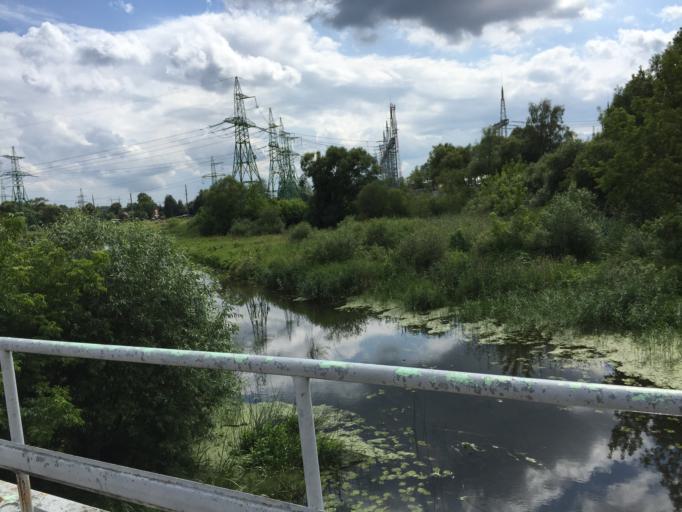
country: LV
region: Jelgava
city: Jelgava
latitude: 56.6294
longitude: 23.7286
